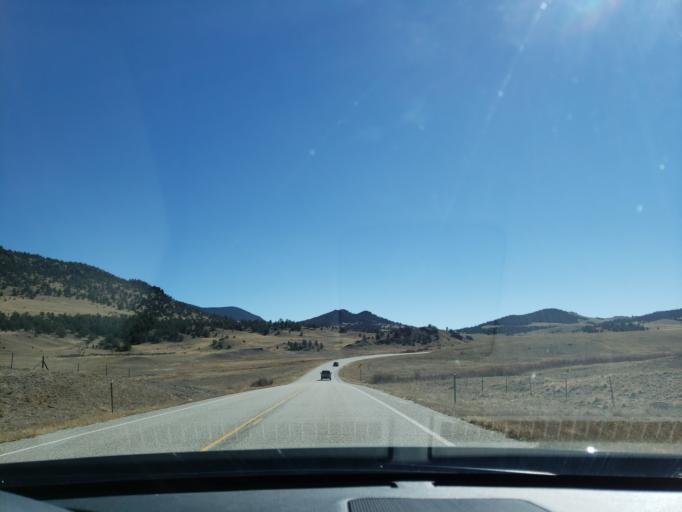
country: US
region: Colorado
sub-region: Chaffee County
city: Salida
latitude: 38.8607
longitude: -105.6566
